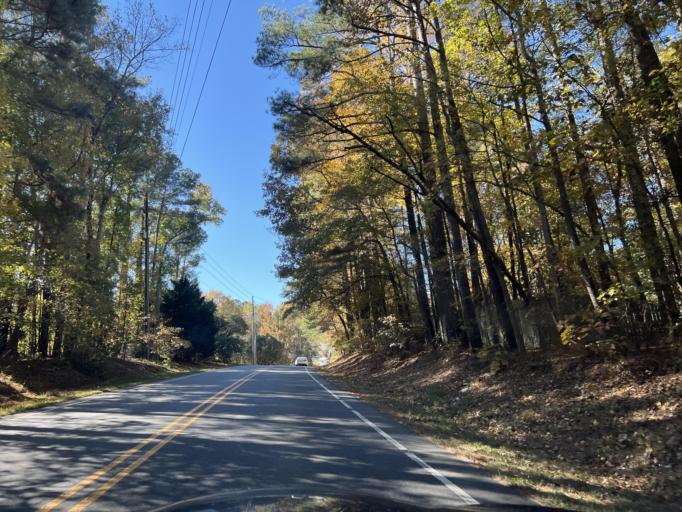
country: US
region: North Carolina
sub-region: Wake County
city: Garner
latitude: 35.6661
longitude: -78.7127
